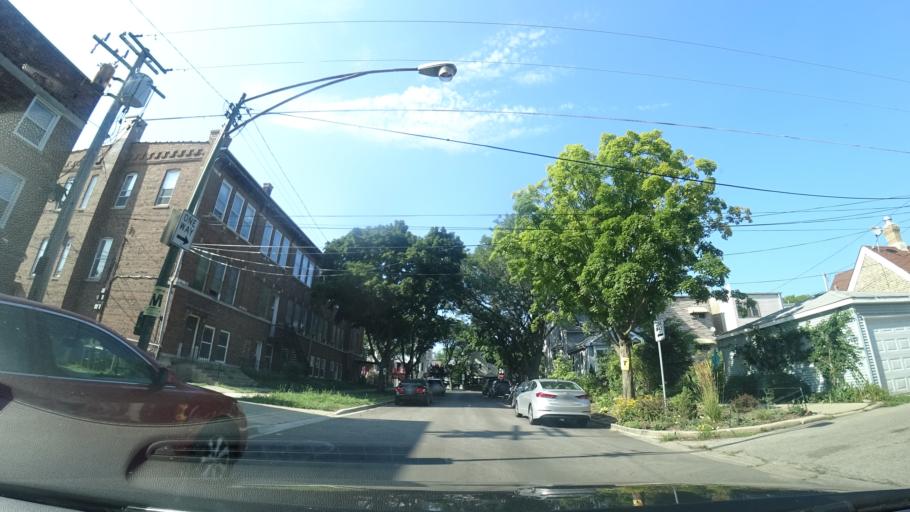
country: US
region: Illinois
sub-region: Cook County
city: Lincolnwood
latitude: 41.9734
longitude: -87.6939
